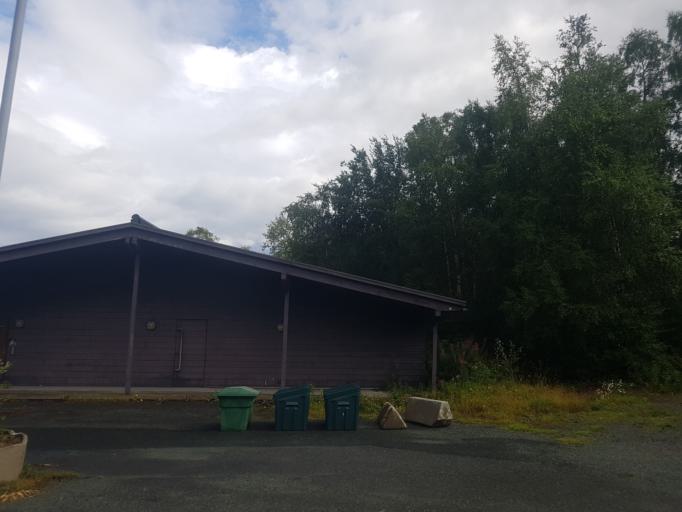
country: NO
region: Sor-Trondelag
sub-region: Trondheim
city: Trondheim
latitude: 63.4088
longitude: 10.4719
